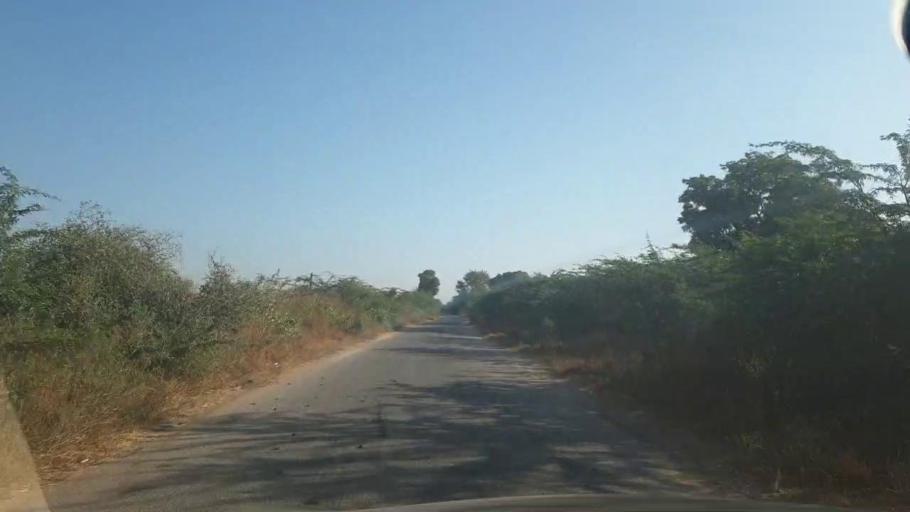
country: PK
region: Sindh
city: Malir Cantonment
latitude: 25.1061
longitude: 67.2604
